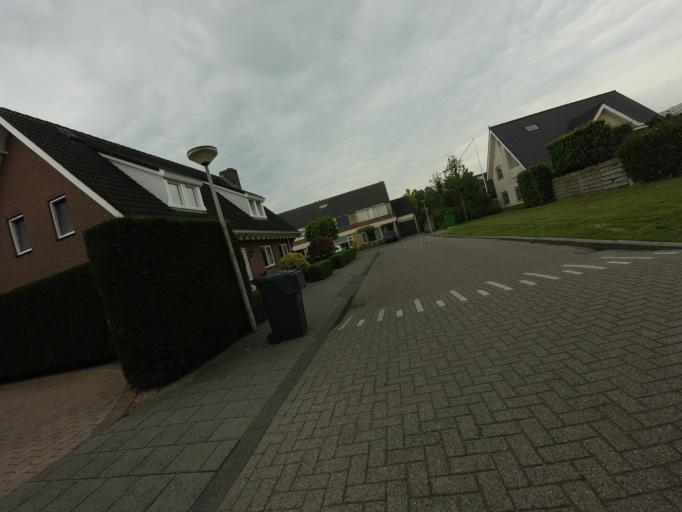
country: NL
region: South Holland
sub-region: Gemeente Spijkenisse
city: Spijkenisse
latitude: 51.8142
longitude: 4.3459
